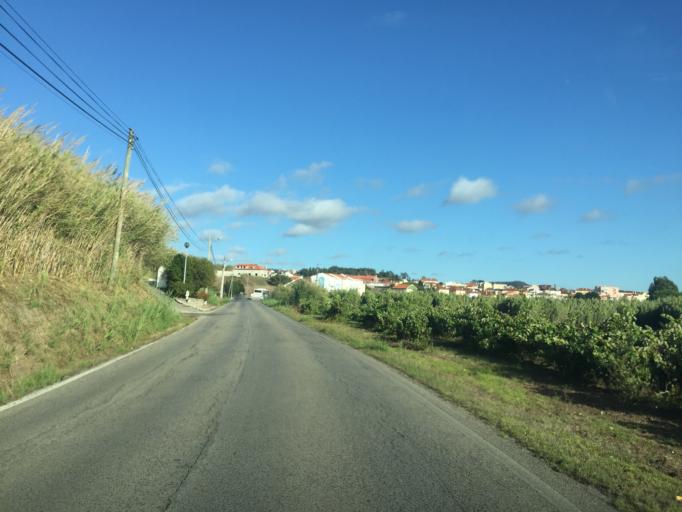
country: PT
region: Lisbon
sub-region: Torres Vedras
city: A dos Cunhados
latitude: 39.1578
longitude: -9.3023
